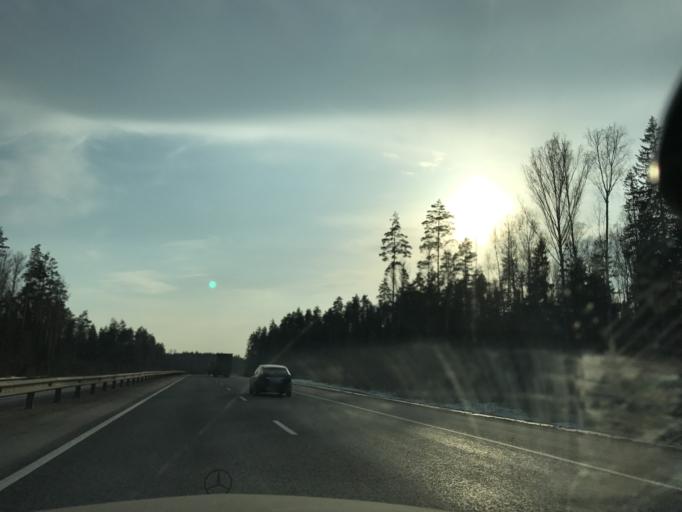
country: RU
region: Vladimir
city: Sudogda
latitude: 56.1544
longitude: 40.9216
